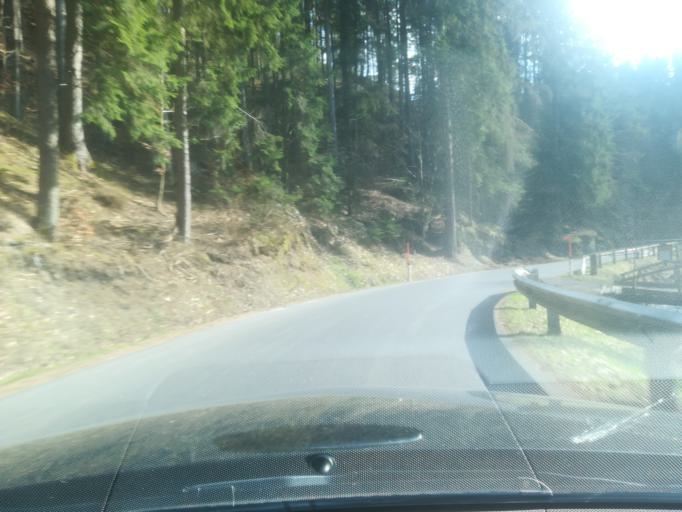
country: AT
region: Upper Austria
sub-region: Politischer Bezirk Freistadt
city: Freistadt
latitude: 48.4166
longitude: 14.6390
